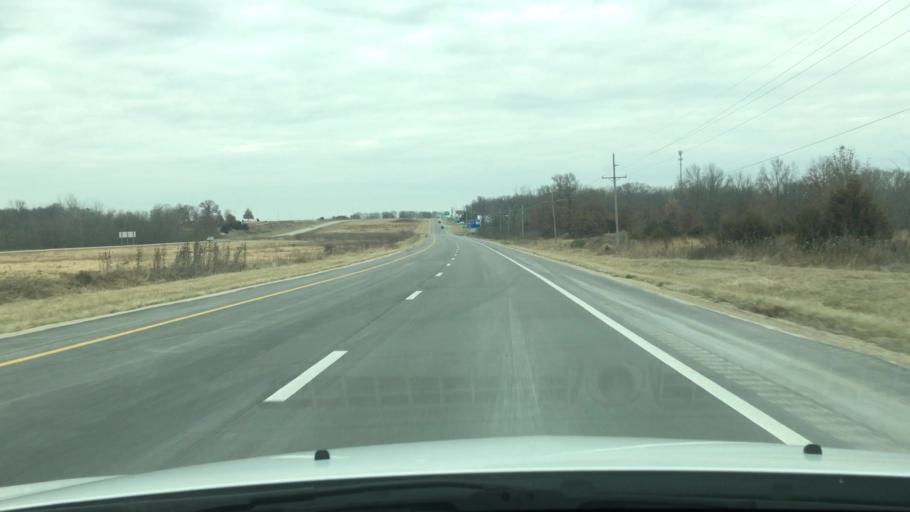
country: US
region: Missouri
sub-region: Audrain County
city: Mexico
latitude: 39.1037
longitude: -91.8961
